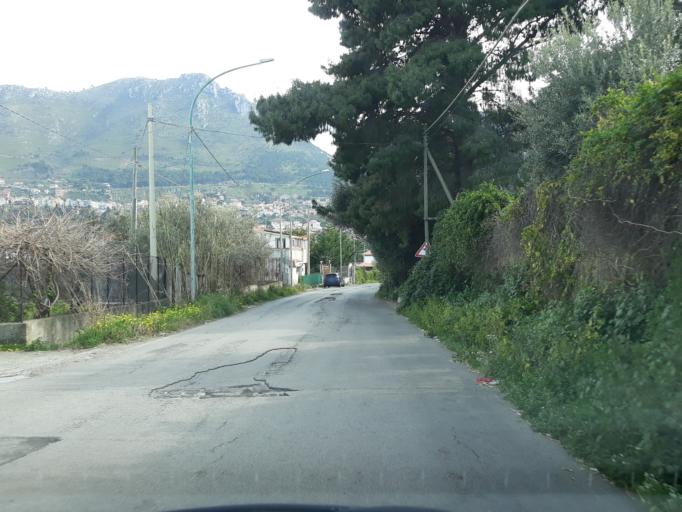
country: IT
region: Sicily
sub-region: Palermo
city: Piano Maglio-Blandino
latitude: 38.0698
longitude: 13.3048
